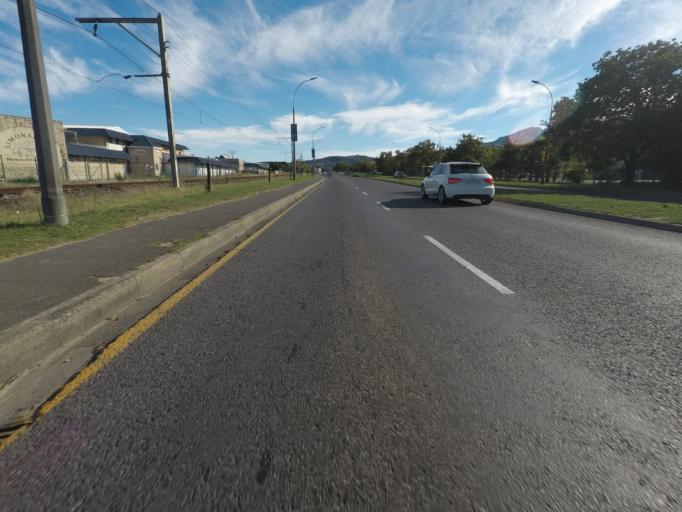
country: ZA
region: Western Cape
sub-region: Cape Winelands District Municipality
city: Stellenbosch
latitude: -33.9295
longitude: 18.8537
